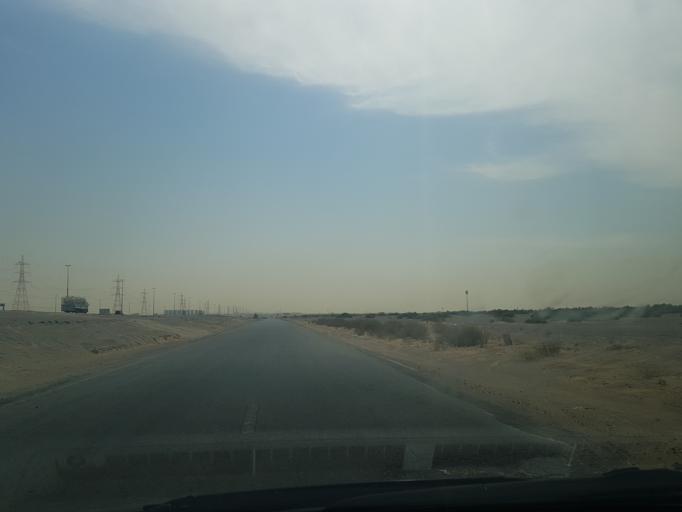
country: AE
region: Ash Shariqah
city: Sharjah
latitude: 25.2856
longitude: 55.5875
